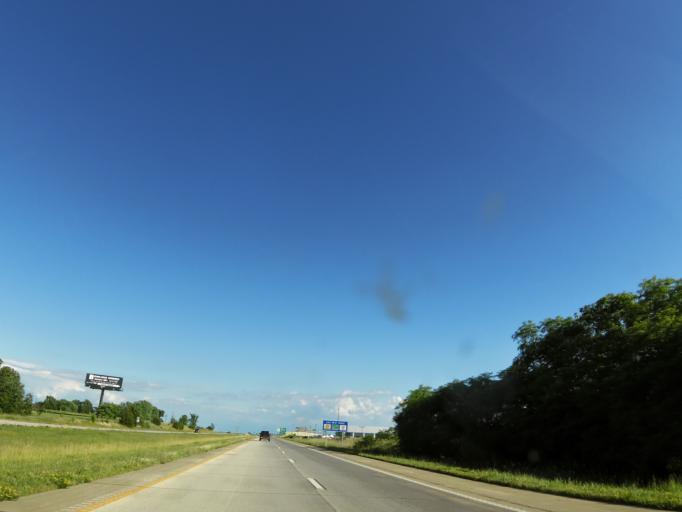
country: US
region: Missouri
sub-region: Pike County
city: Bowling Green
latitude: 39.3416
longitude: -91.1830
